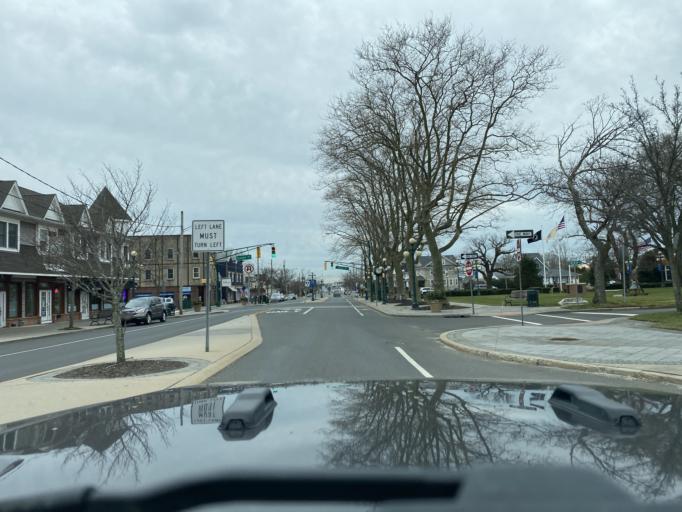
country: US
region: New Jersey
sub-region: Monmouth County
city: Avon-by-the-Sea
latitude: 40.1914
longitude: -74.0222
